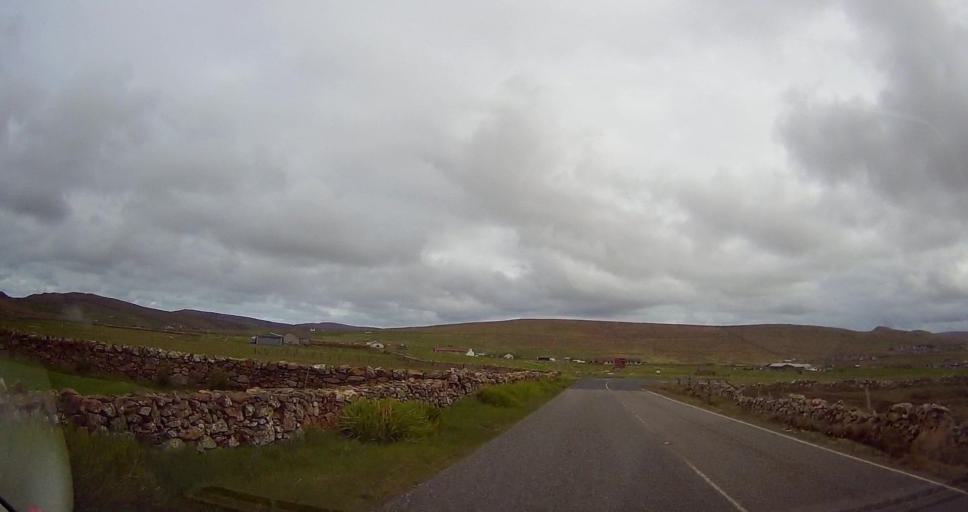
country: GB
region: Scotland
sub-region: Shetland Islands
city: Shetland
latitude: 60.7533
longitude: -0.8850
